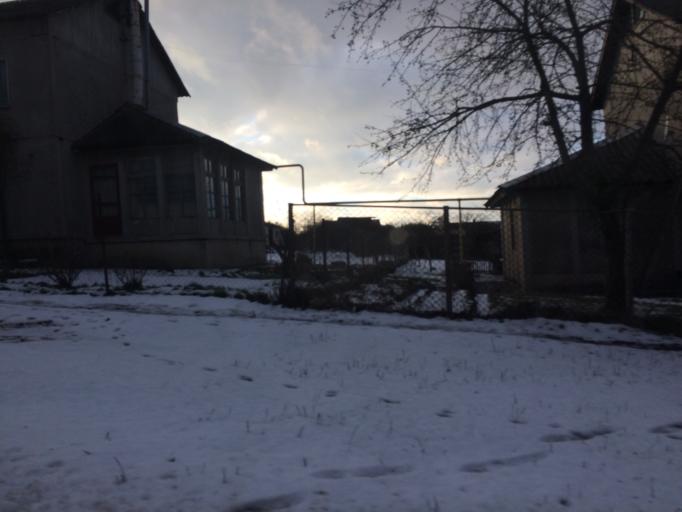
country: RU
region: Tula
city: Cherepet'
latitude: 54.1119
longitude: 36.3272
